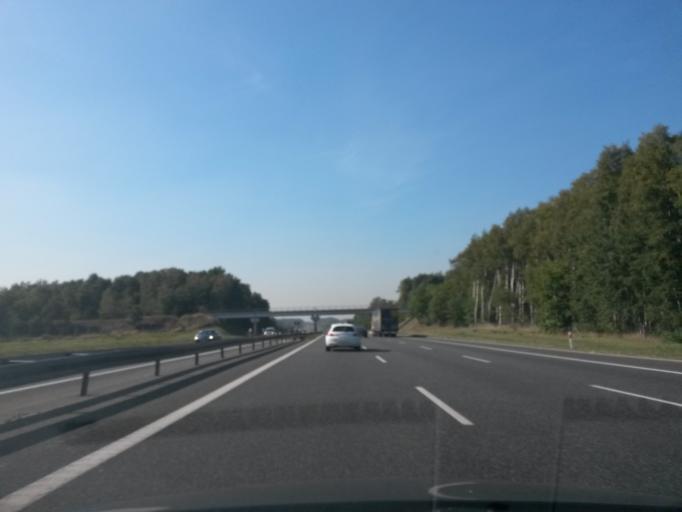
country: PL
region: Silesian Voivodeship
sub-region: Ruda Slaska
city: Ruda Slaska
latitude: 50.2587
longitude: 18.8339
